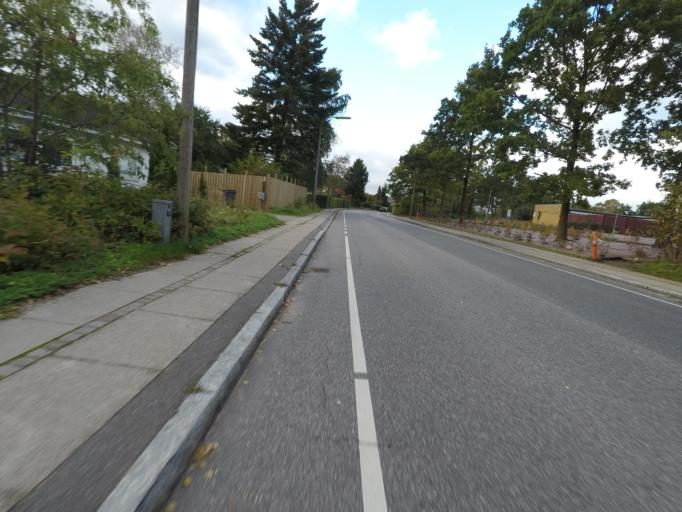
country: DK
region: Capital Region
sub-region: Ballerup Kommune
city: Ballerup
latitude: 55.7507
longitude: 12.3936
